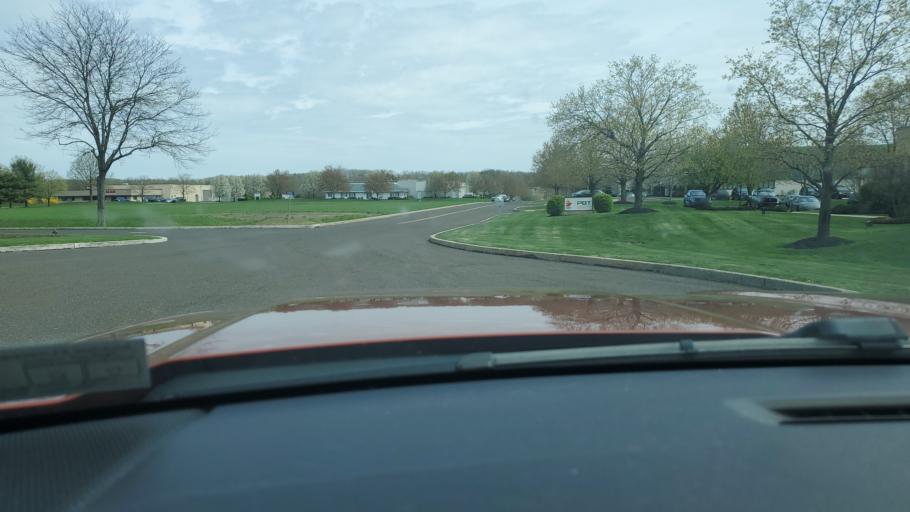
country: US
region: Pennsylvania
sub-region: Montgomery County
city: Hatfield
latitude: 40.2858
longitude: -75.2801
